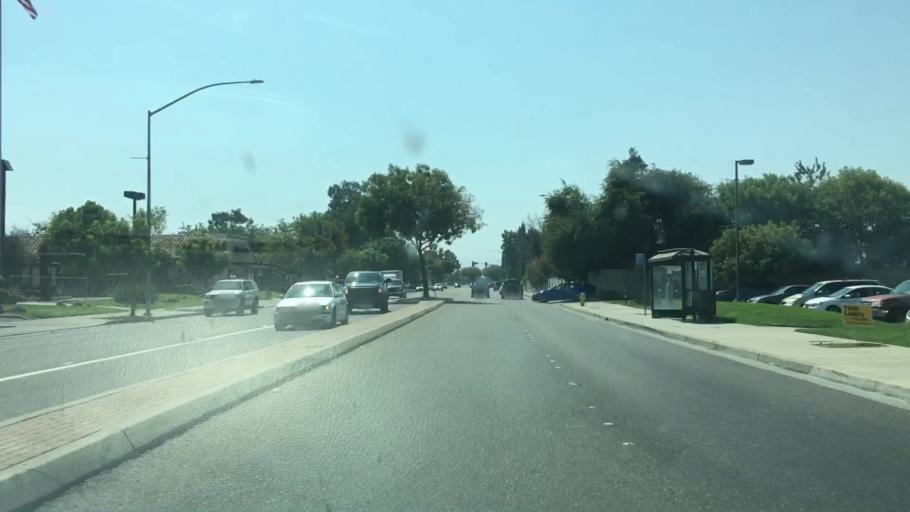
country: US
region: California
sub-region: San Joaquin County
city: Tracy
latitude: 37.7602
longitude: -121.4351
